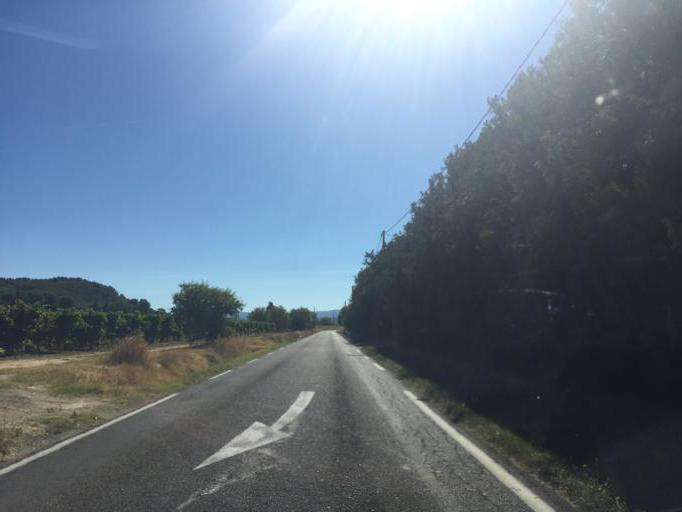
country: FR
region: Provence-Alpes-Cote d'Azur
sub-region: Departement du Vaucluse
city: Saint-Didier
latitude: 44.0283
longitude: 5.0877
